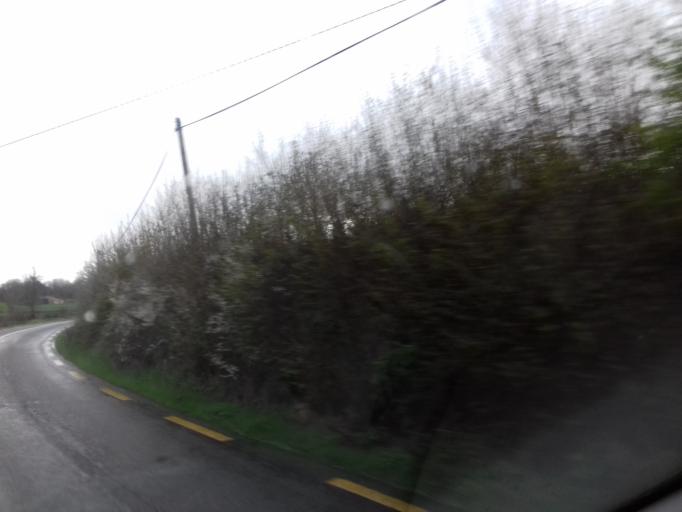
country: IE
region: Connaught
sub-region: County Leitrim
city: Manorhamilton
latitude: 54.2735
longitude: -7.9372
